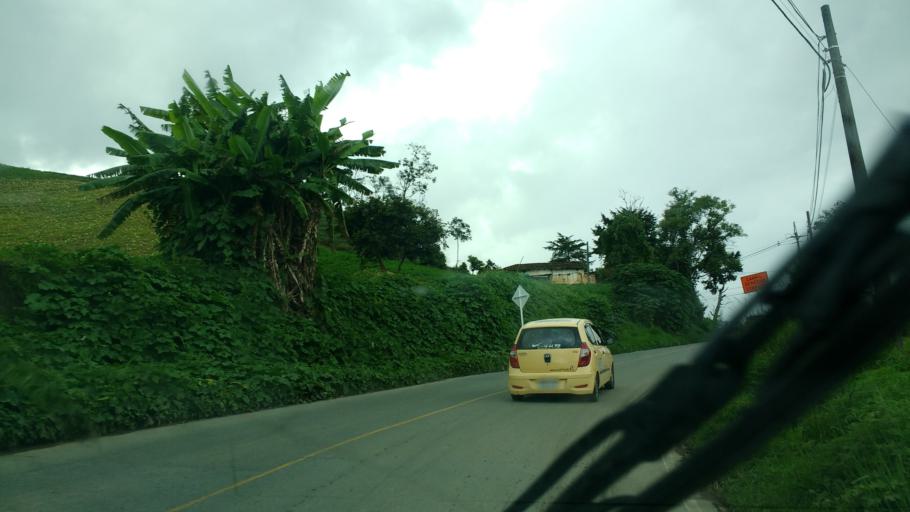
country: CO
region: Antioquia
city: Marinilla
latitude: 6.1758
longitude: -75.3174
